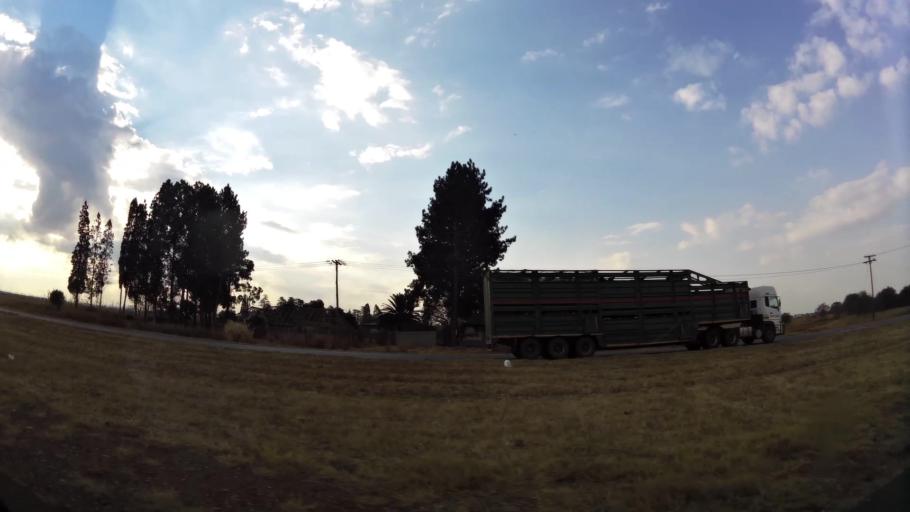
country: ZA
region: Gauteng
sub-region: Sedibeng District Municipality
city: Vanderbijlpark
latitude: -26.6195
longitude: 27.8179
